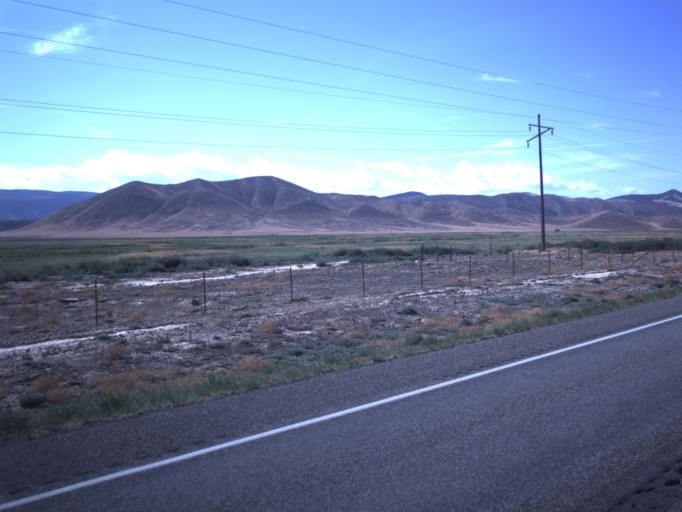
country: US
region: Utah
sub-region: Sevier County
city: Salina
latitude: 39.0375
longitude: -111.8277
